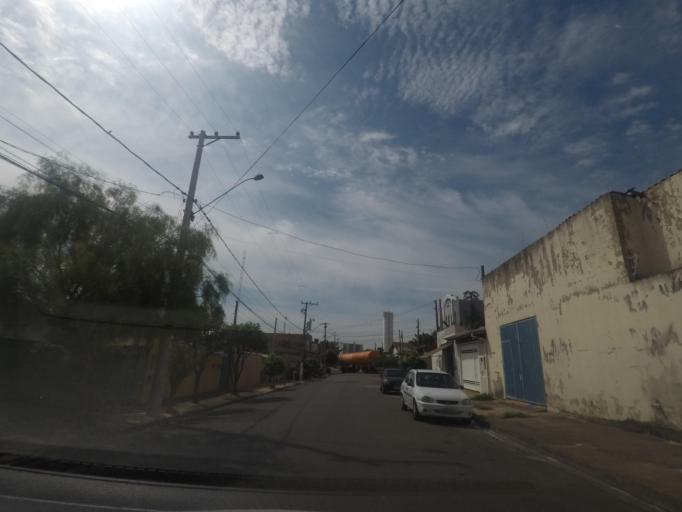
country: BR
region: Sao Paulo
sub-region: Sumare
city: Sumare
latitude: -22.8038
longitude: -47.2464
